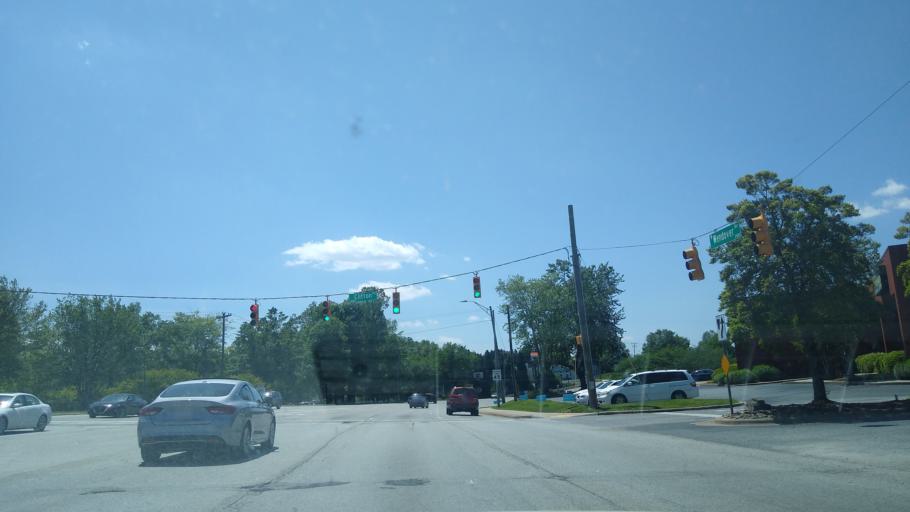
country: US
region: North Carolina
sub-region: Guilford County
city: Greensboro
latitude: 36.0607
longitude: -79.8628
